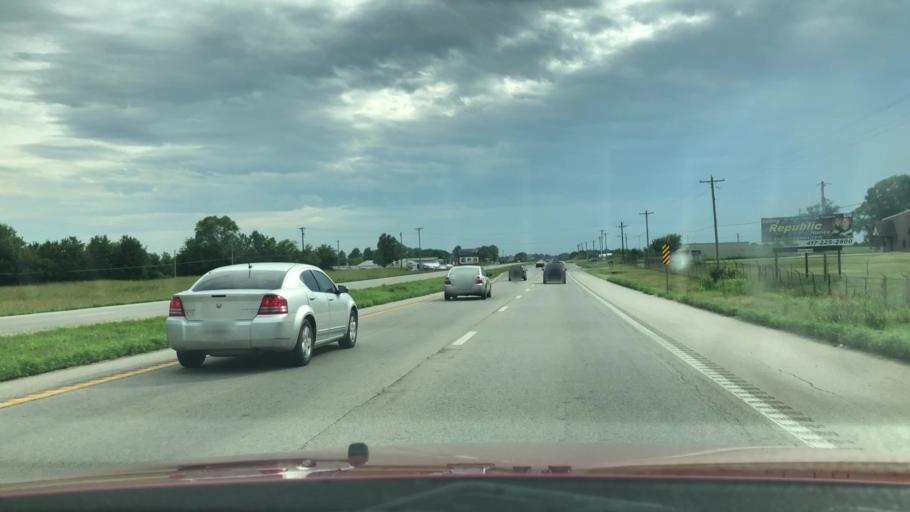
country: US
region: Missouri
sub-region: Greene County
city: Battlefield
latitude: 37.1558
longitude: -93.4100
